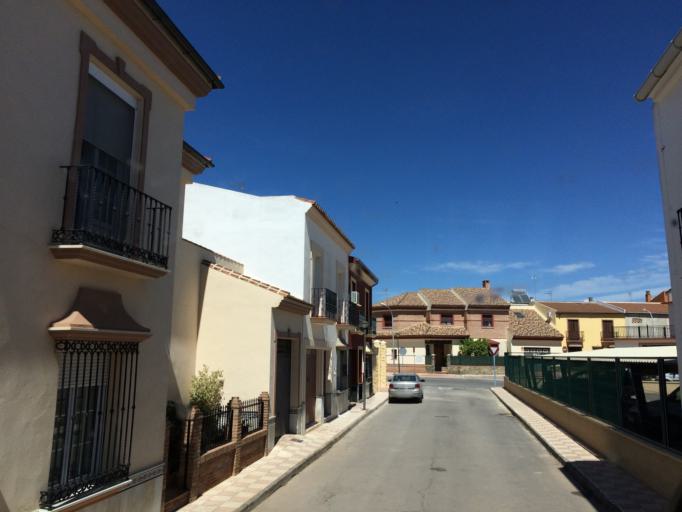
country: ES
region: Andalusia
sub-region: Provincia de Malaga
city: Campillos
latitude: 37.0457
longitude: -4.8665
